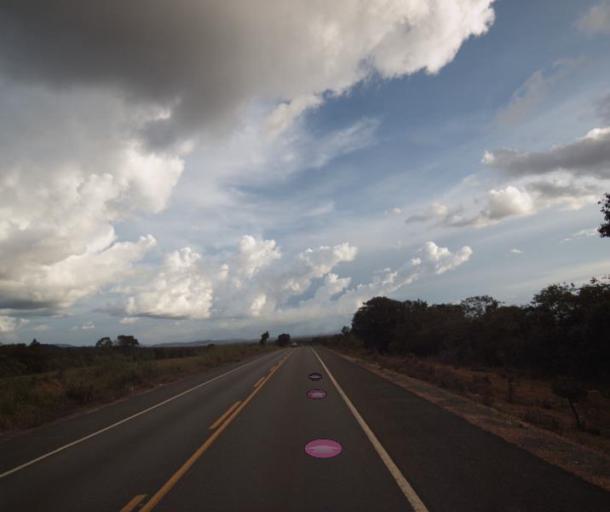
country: BR
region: Goias
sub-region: Niquelandia
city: Niquelandia
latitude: -14.7138
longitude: -48.6062
